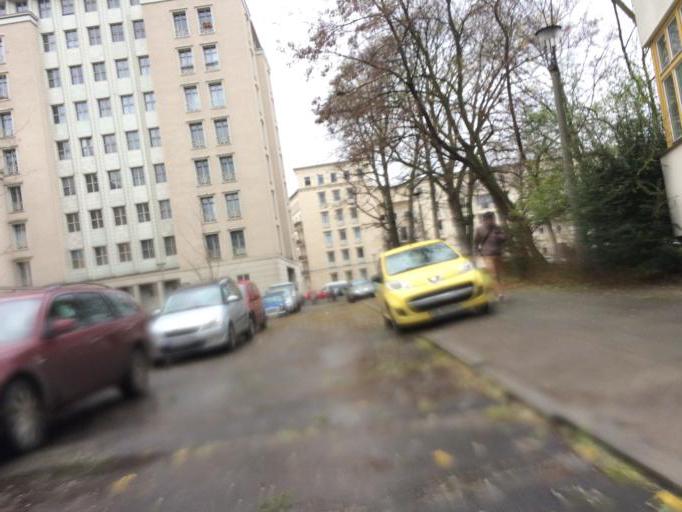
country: DE
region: Berlin
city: Friedrichshain Bezirk
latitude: 52.5154
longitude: 13.4445
